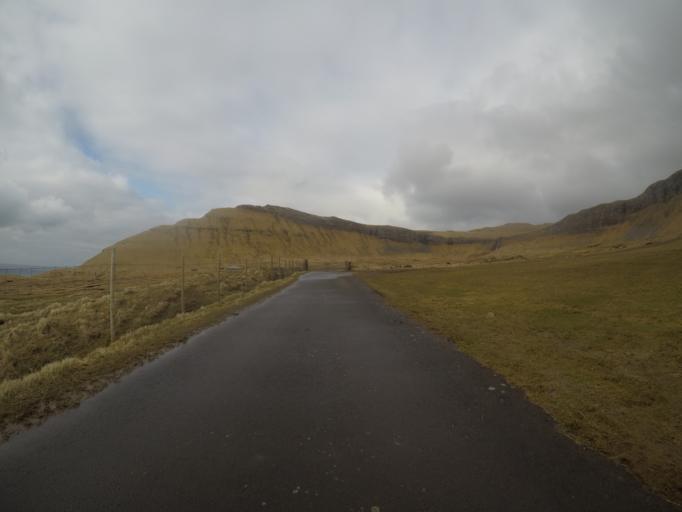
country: FO
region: Streymoy
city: Kollafjordhur
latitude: 62.0402
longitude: -6.9597
